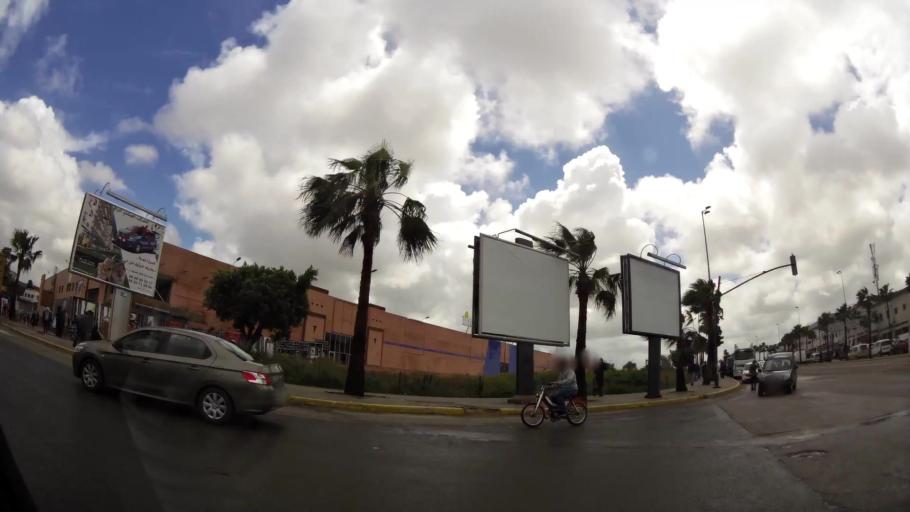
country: MA
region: Grand Casablanca
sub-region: Casablanca
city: Casablanca
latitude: 33.5623
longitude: -7.5947
